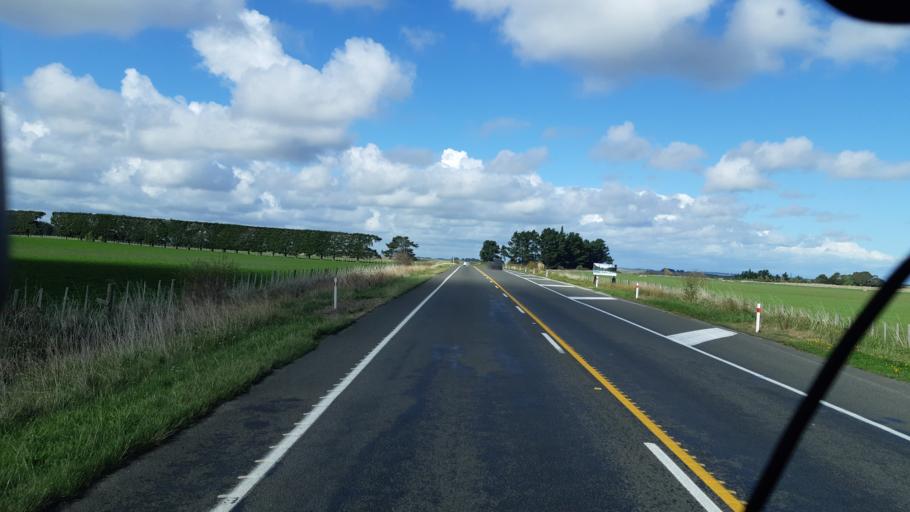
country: NZ
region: Manawatu-Wanganui
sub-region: Wanganui District
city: Wanganui
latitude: -39.9914
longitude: 175.1647
